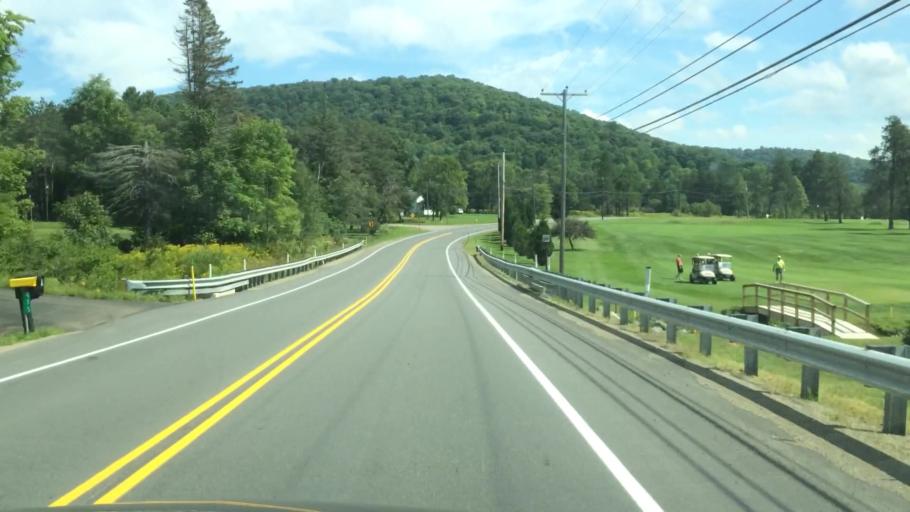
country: US
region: Pennsylvania
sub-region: McKean County
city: Bradford
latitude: 41.9043
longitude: -78.6144
